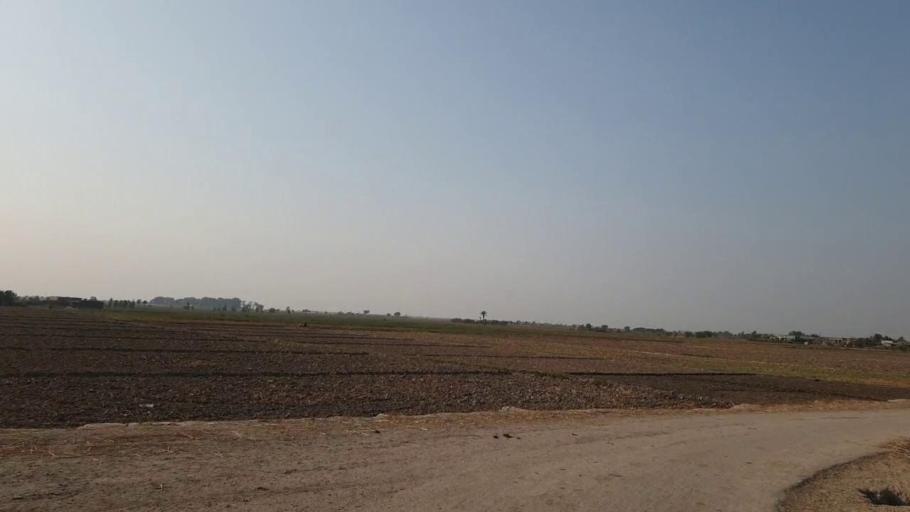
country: PK
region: Sindh
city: Bulri
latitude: 24.9995
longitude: 68.3775
